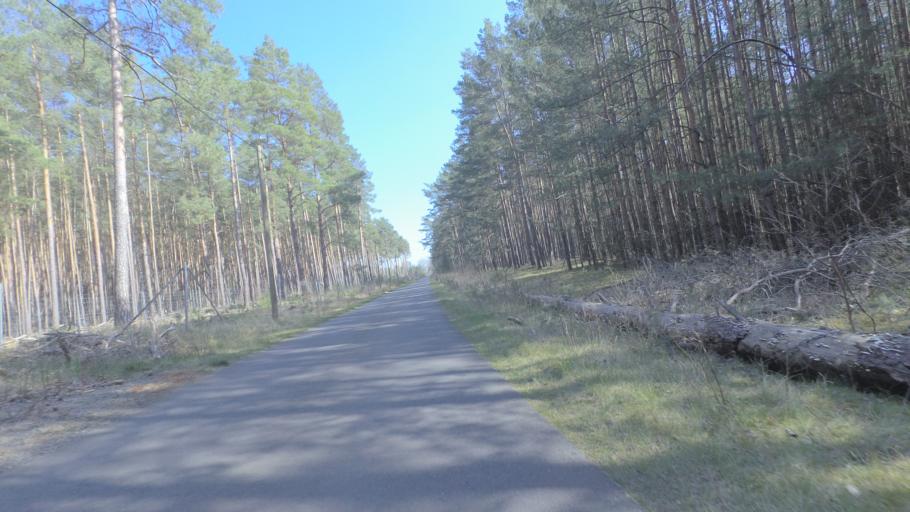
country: DE
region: Brandenburg
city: Munchehofe
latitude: 52.1621
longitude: 13.7848
